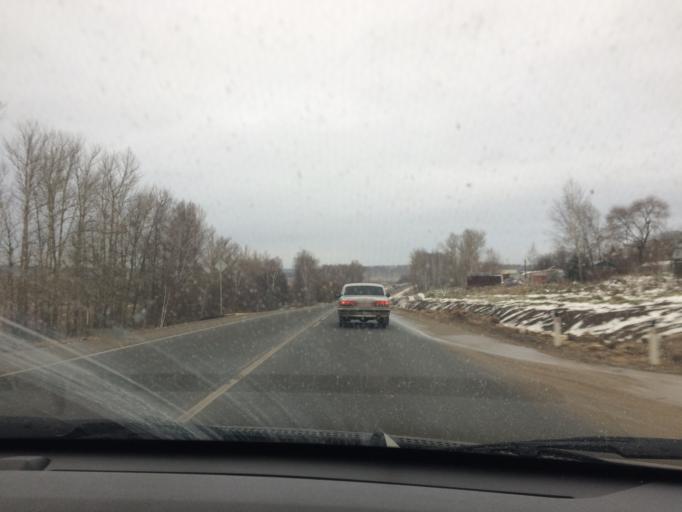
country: RU
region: Tula
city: Gorelki
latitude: 54.2410
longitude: 37.6618
